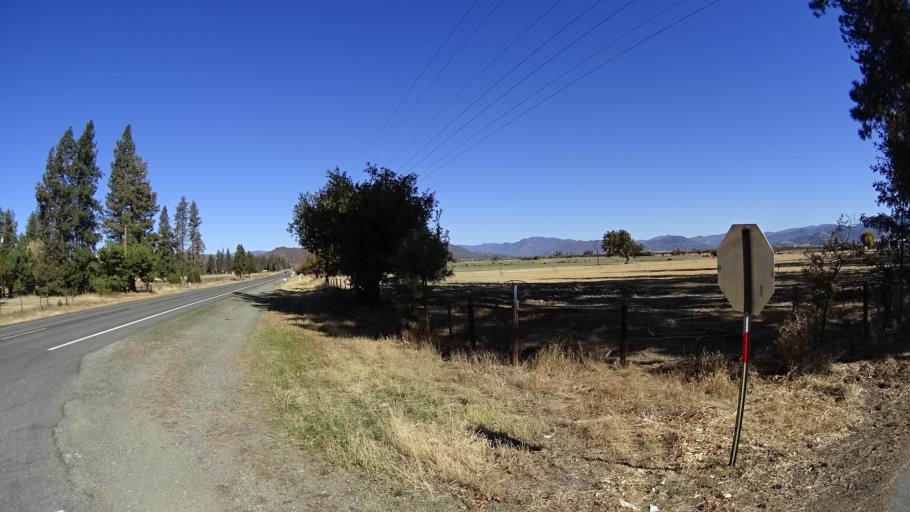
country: US
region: California
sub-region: Siskiyou County
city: Yreka
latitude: 41.5248
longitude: -122.9066
